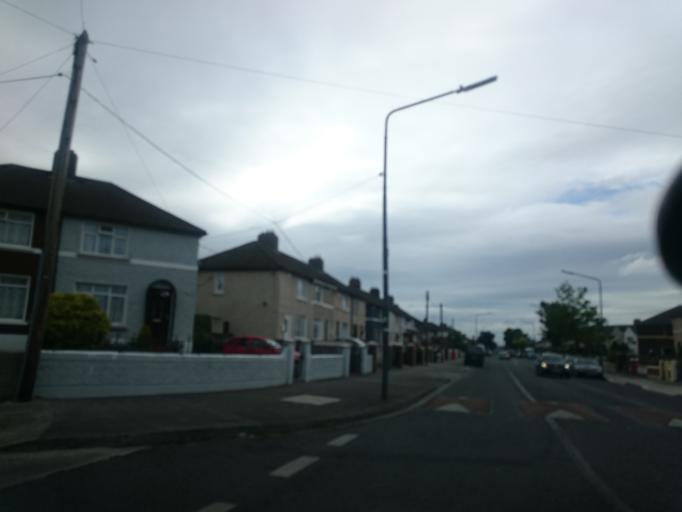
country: IE
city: Greenhills
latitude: 53.3233
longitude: -6.3013
